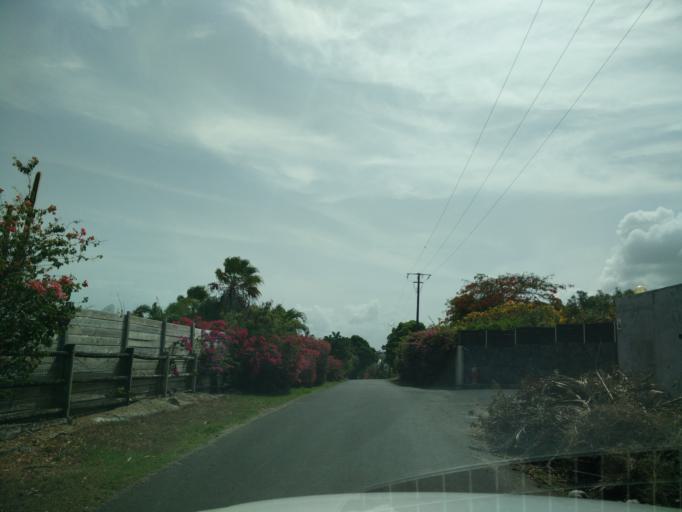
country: GP
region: Guadeloupe
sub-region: Guadeloupe
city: Sainte-Anne
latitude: 16.2432
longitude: -61.3338
